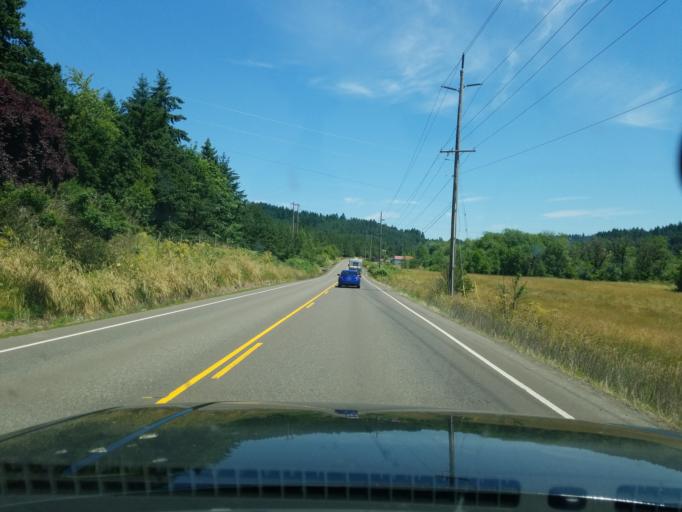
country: US
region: Oregon
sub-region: Yamhill County
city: Yamhill
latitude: 45.3692
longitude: -123.1621
